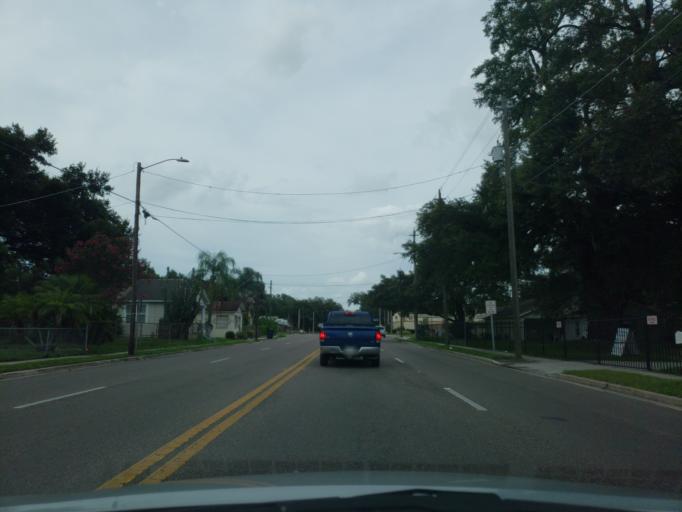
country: US
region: Florida
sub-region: Hillsborough County
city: Tampa
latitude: 27.9797
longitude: -82.4429
